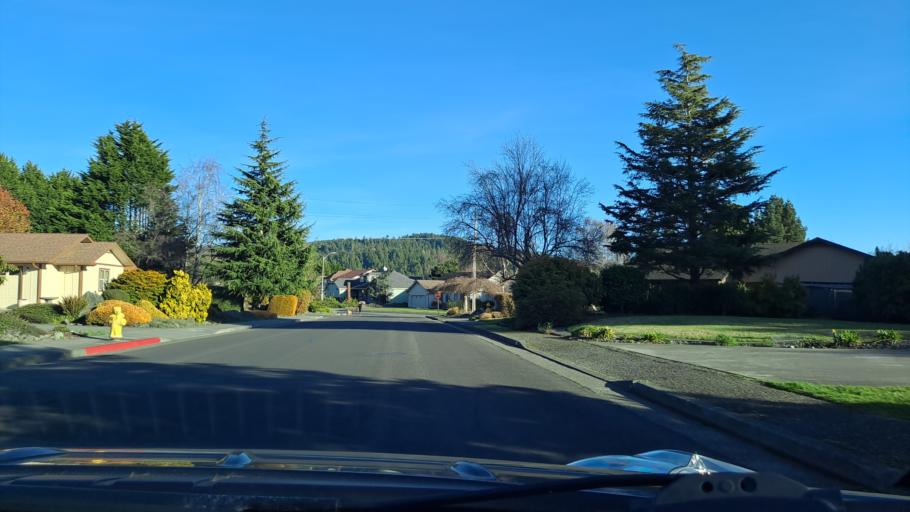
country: US
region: California
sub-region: Humboldt County
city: Fortuna
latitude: 40.5966
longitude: -124.1372
